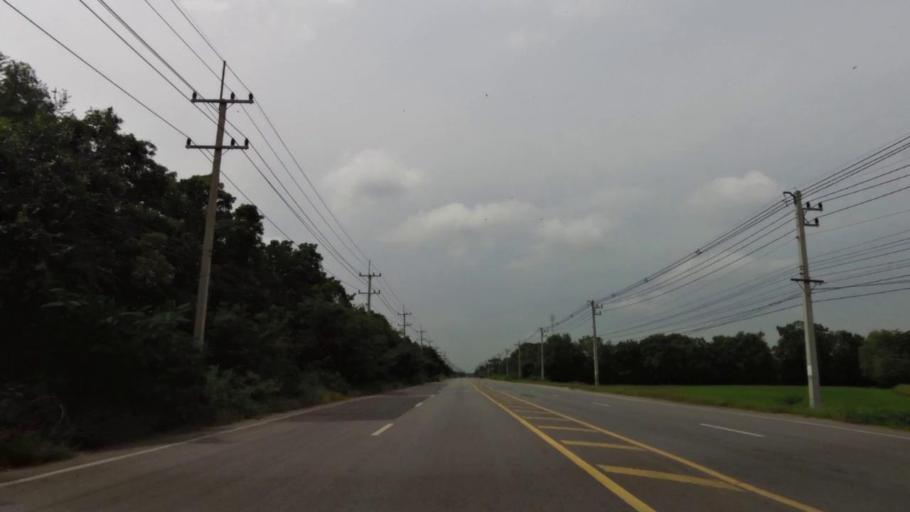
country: TH
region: Lop Buri
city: Ban Mi
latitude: 15.0628
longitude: 100.6101
